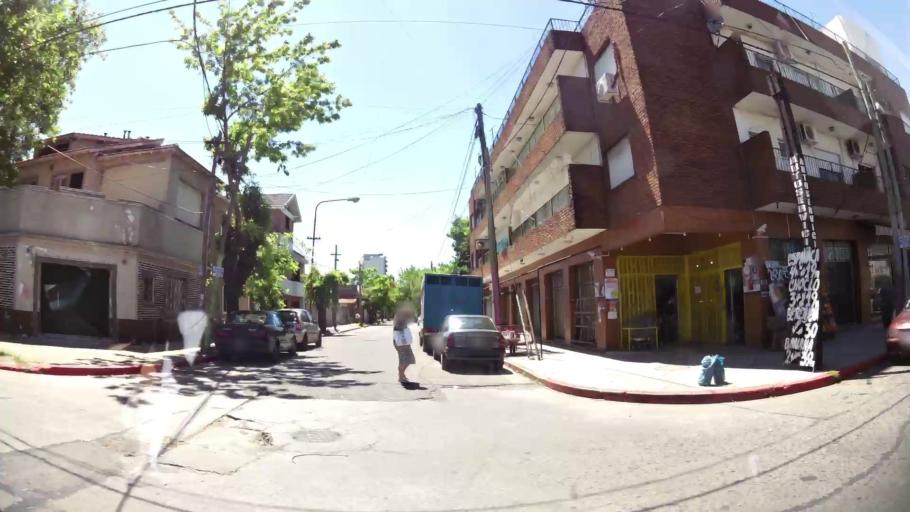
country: AR
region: Buenos Aires
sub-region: Partido de Quilmes
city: Quilmes
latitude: -34.7149
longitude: -58.2767
